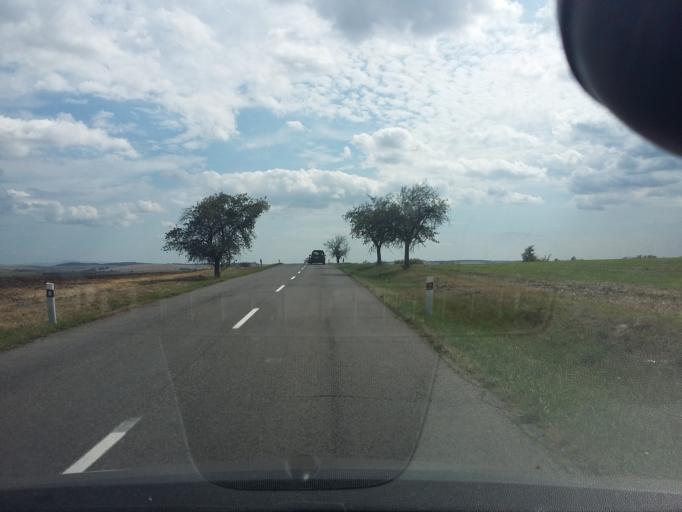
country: SK
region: Trnavsky
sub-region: Okres Skalica
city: Holic
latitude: 48.7572
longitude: 17.1715
